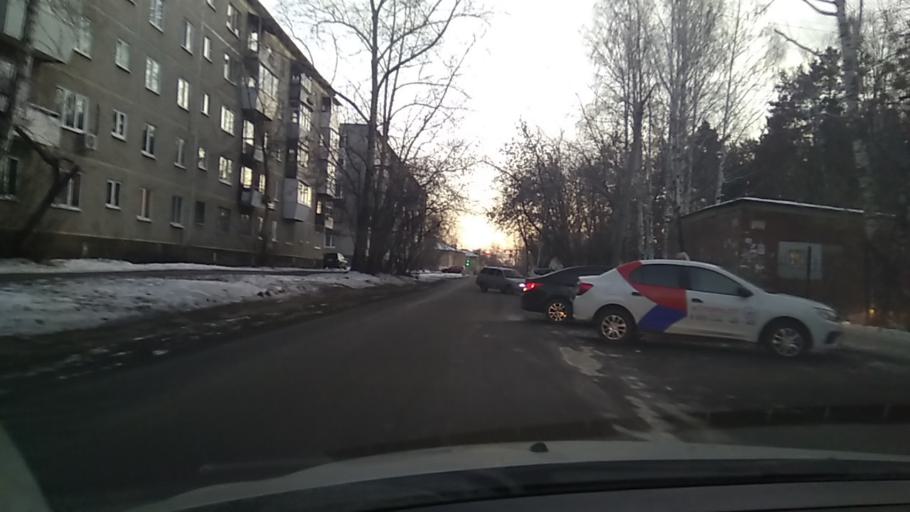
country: RU
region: Sverdlovsk
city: Istok
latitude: 56.7640
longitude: 60.7109
